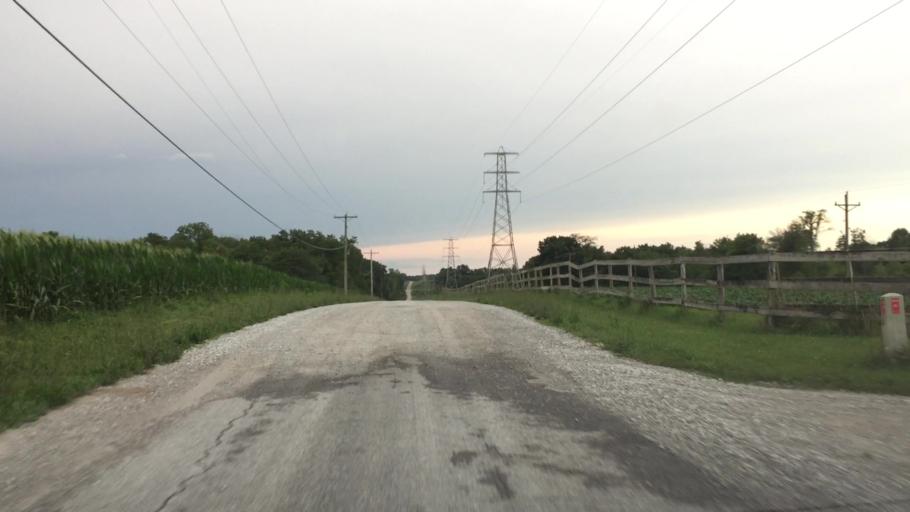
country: US
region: Illinois
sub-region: Hancock County
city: Hamilton
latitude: 40.3712
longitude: -91.3613
